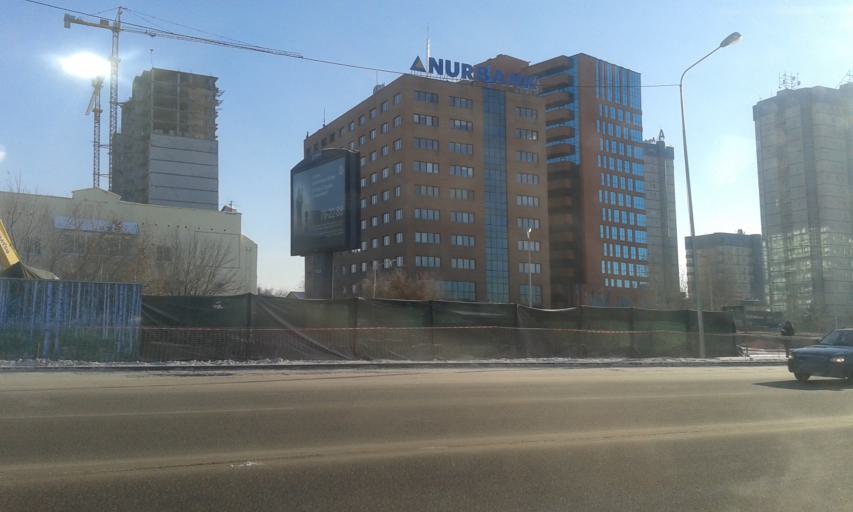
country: KZ
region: Astana Qalasy
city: Astana
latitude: 51.1487
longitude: 71.4235
